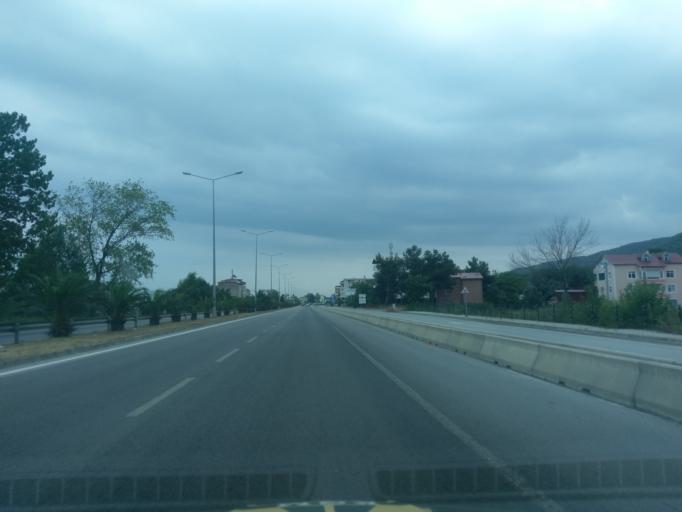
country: TR
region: Samsun
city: Taflan
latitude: 41.4032
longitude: 36.1868
